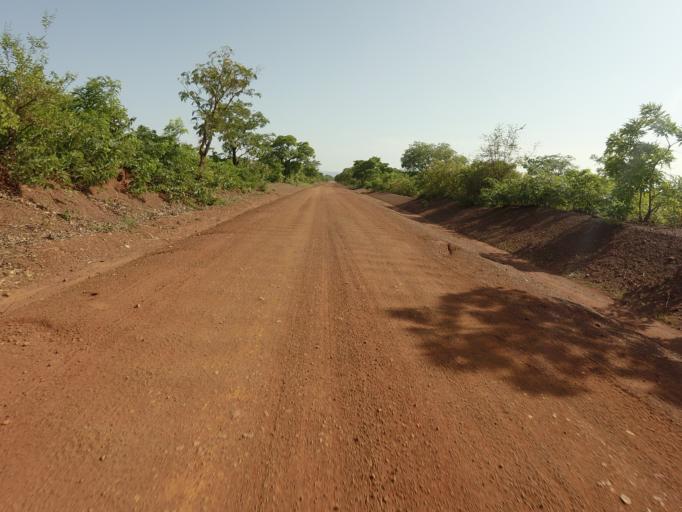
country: GH
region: Upper East
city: Bawku
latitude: 10.7356
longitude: -0.2027
